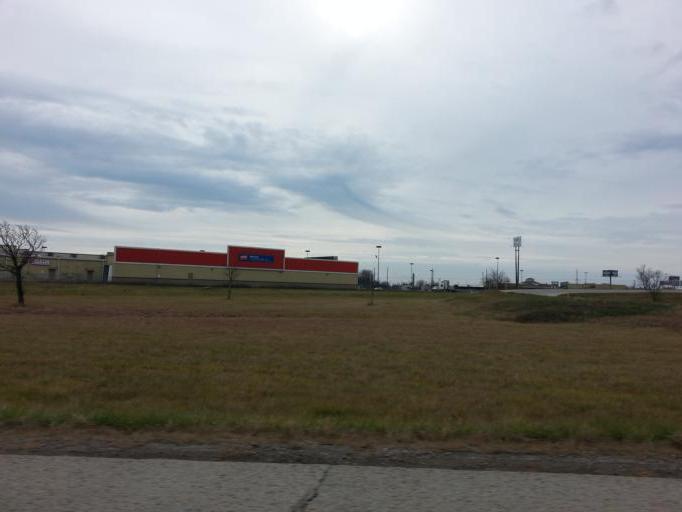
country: US
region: Indiana
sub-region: Decatur County
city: Greensburg
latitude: 39.3622
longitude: -85.4777
